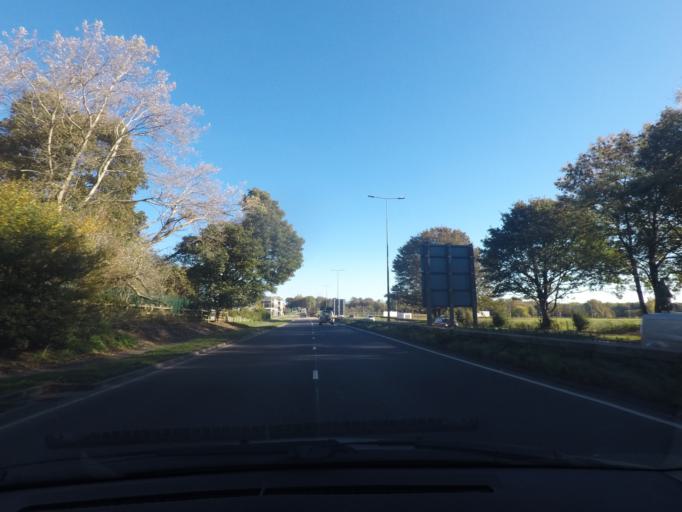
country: GB
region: England
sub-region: East Riding of Yorkshire
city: Hessle
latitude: 53.7227
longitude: -0.4623
